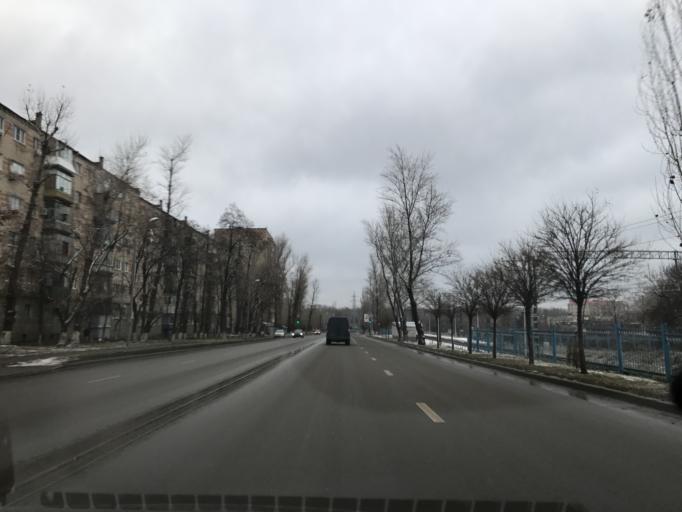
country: RU
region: Rostov
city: Imeni Chkalova
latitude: 47.2609
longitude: 39.7852
